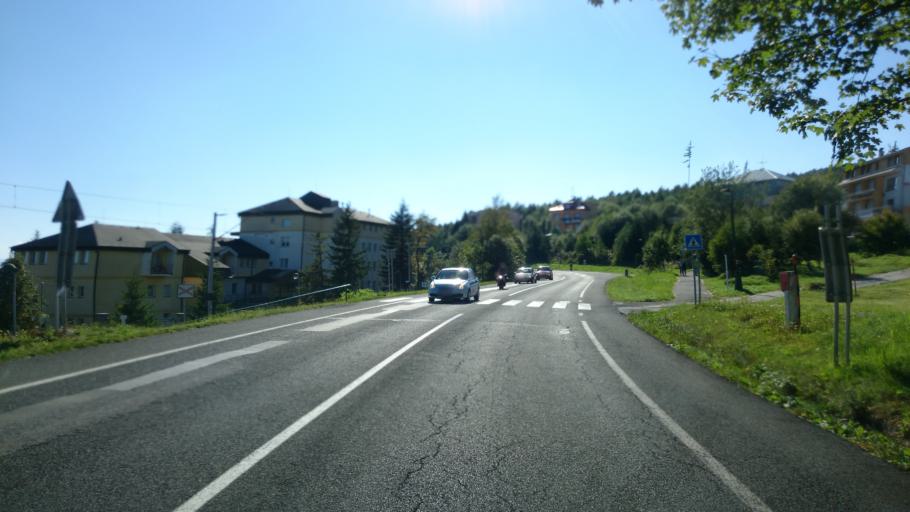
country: SK
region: Presovsky
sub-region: Okres Poprad
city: Vysoke Tatry
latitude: 49.1432
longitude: 20.2416
